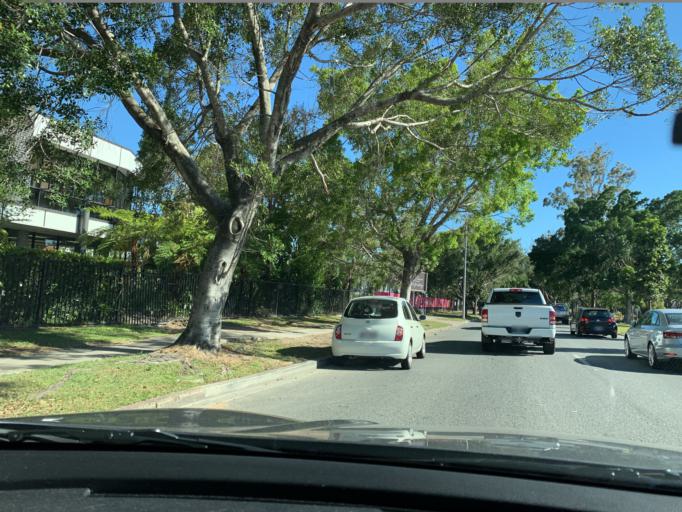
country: AU
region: Queensland
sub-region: Brisbane
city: Ascot
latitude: -27.4319
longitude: 153.0883
